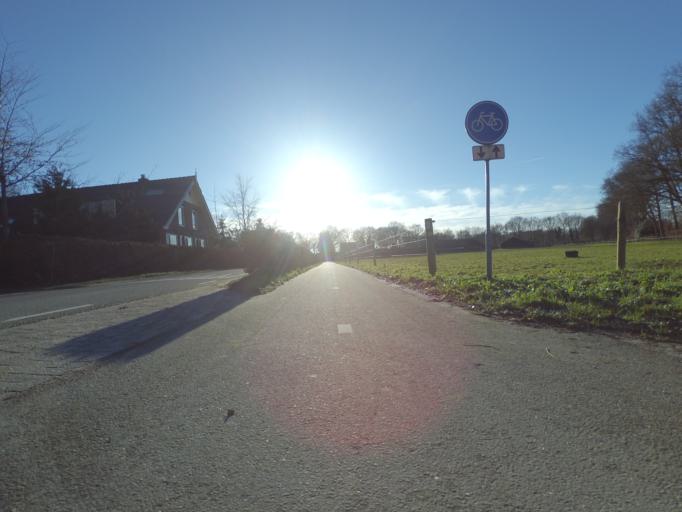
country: NL
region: Gelderland
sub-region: Gemeente Putten
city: Putten
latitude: 52.2656
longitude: 5.6021
